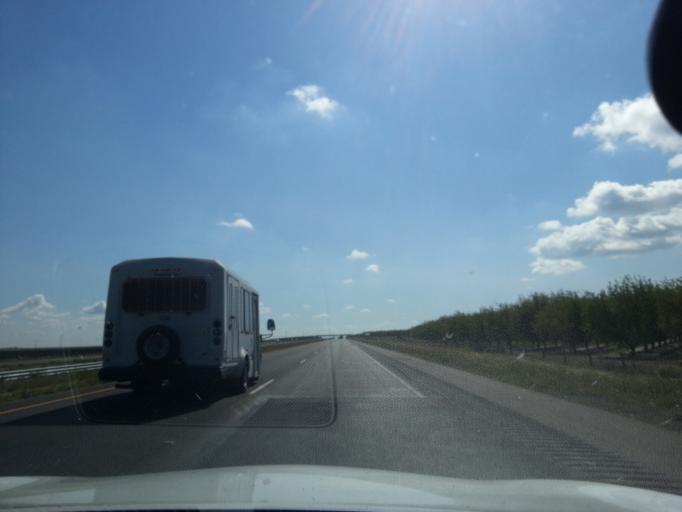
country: US
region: California
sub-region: Fresno County
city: Coalinga
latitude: 36.3796
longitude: -120.3442
